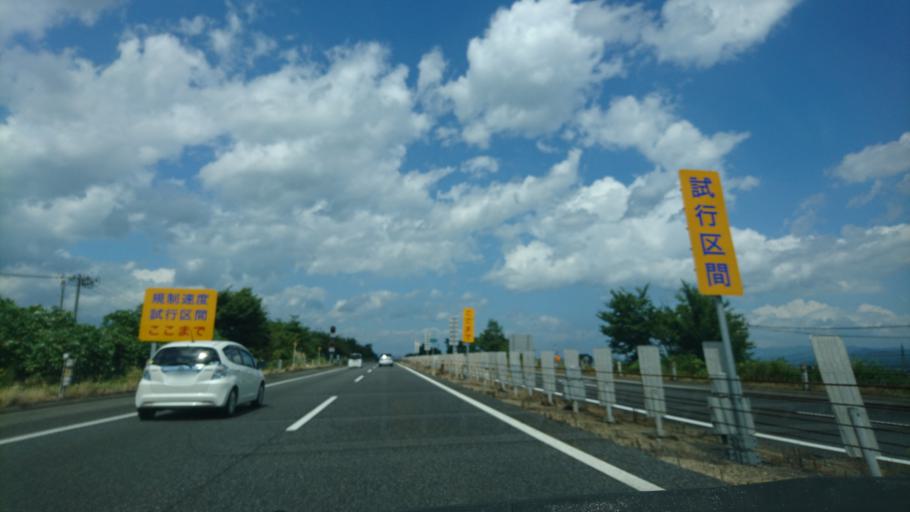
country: JP
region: Iwate
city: Morioka-shi
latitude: 39.6339
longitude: 141.1271
